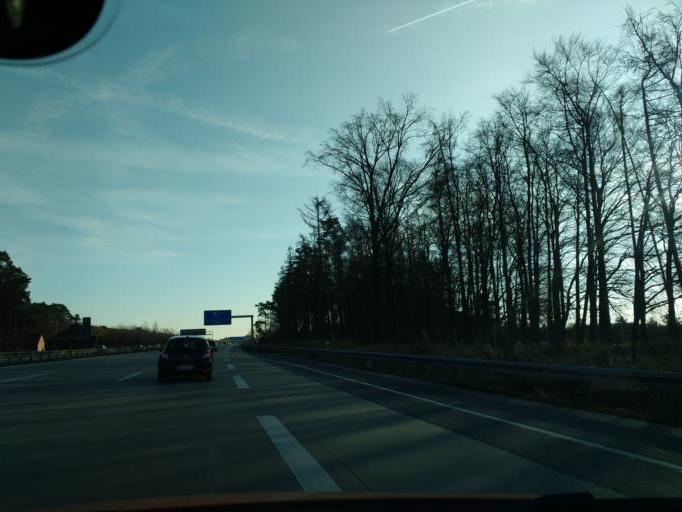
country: DE
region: Brandenburg
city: Ahrensfelde
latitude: 52.6089
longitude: 13.5894
